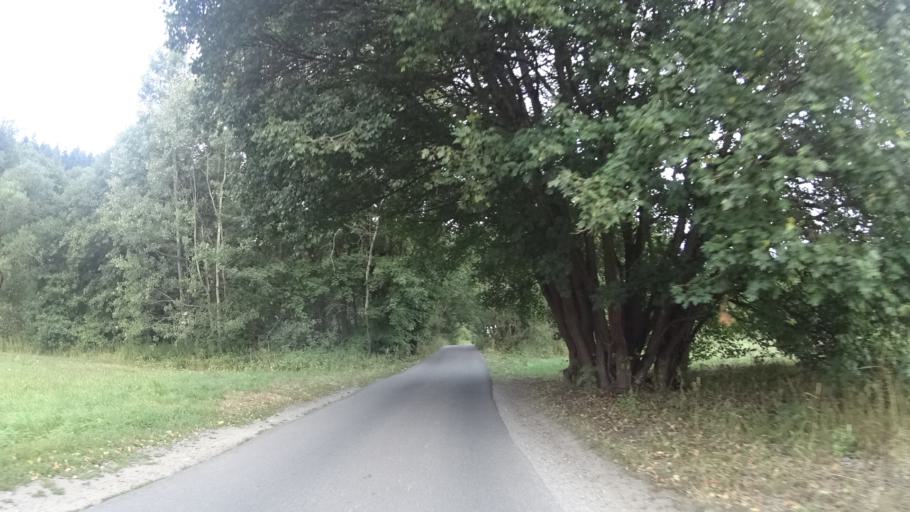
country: CZ
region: Olomoucky
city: Zabreh
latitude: 49.8667
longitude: 16.7928
